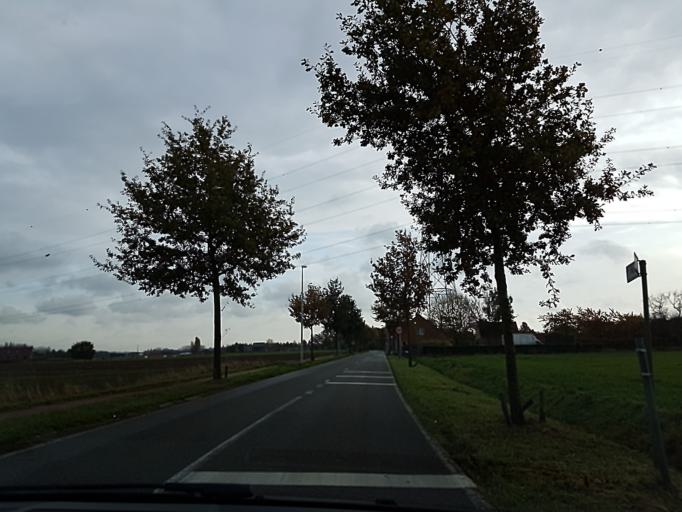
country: BE
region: Flanders
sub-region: Provincie Antwerpen
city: Ranst
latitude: 51.1590
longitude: 4.5395
